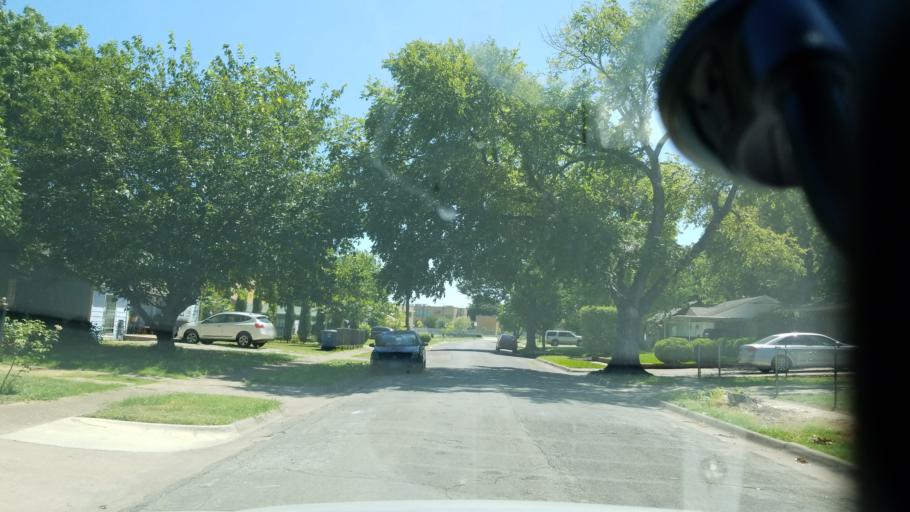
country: US
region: Texas
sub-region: Dallas County
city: Cockrell Hill
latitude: 32.7080
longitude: -96.8262
